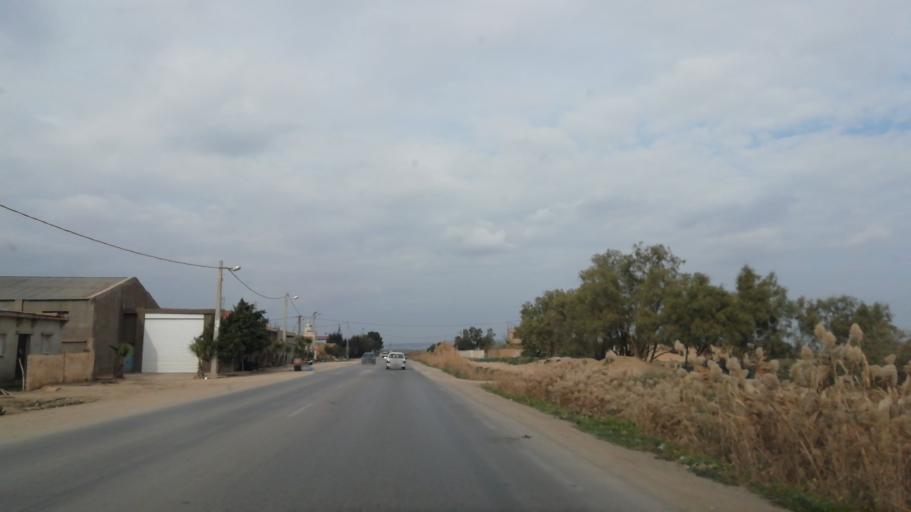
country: DZ
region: Mostaganem
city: Mostaganem
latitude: 35.6964
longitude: 0.0556
